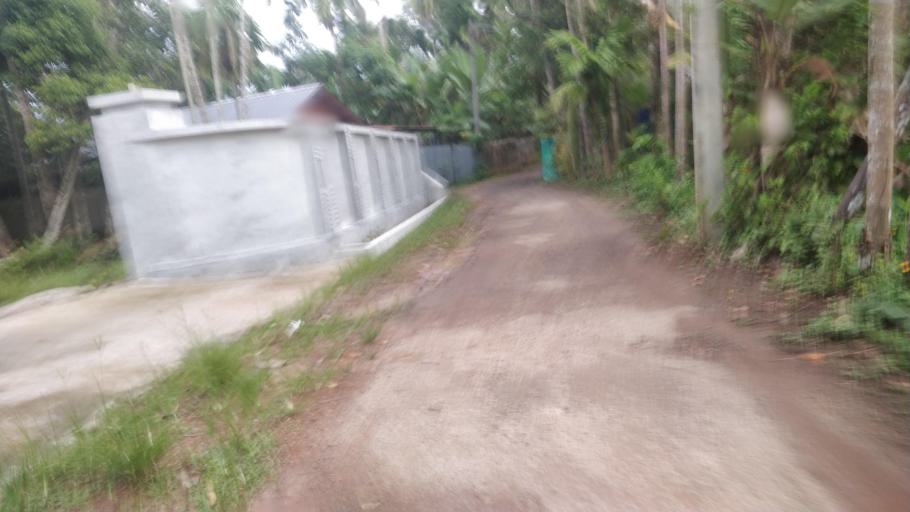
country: IN
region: Kerala
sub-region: Alappuzha
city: Vayalar
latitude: 9.7067
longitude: 76.3514
